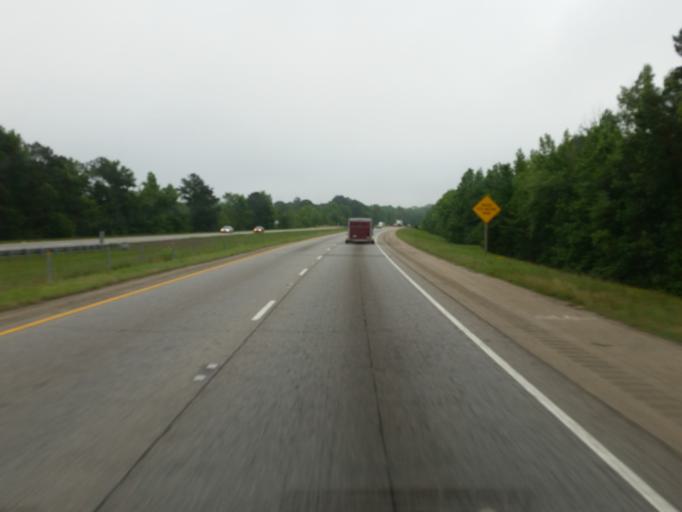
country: US
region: Louisiana
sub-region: Webster Parish
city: Minden
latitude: 32.5941
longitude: -93.3211
